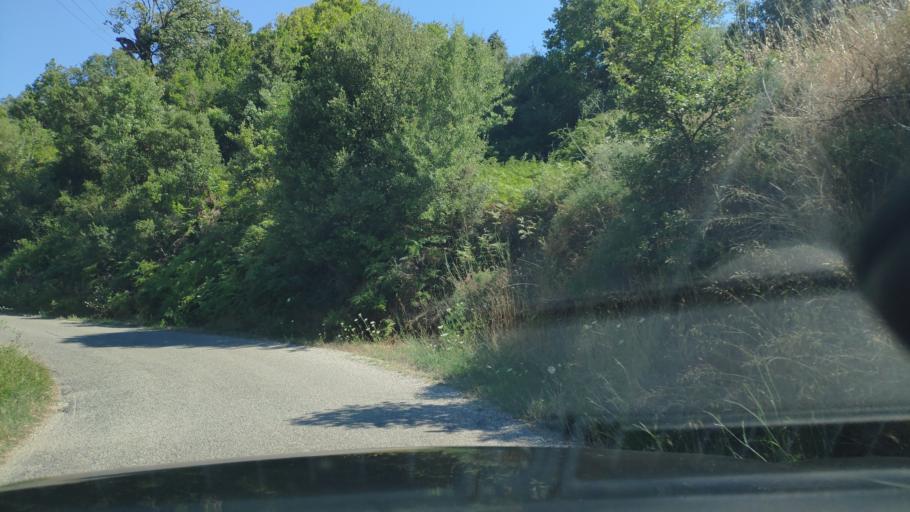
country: GR
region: West Greece
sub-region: Nomos Aitolias kai Akarnanias
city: Katouna
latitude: 38.8361
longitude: 21.0977
